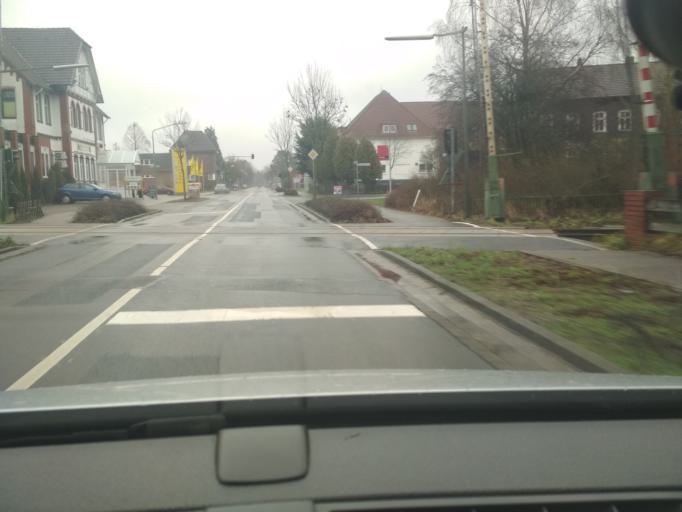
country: DE
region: Lower Saxony
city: Wittingen
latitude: 52.7290
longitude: 10.7242
